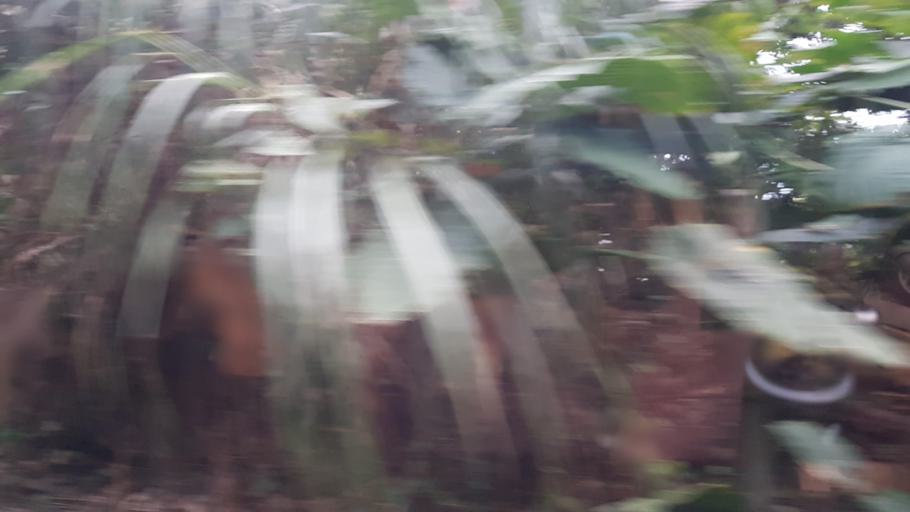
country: TW
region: Taiwan
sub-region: Chiayi
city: Jiayi Shi
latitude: 23.3271
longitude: 120.4867
